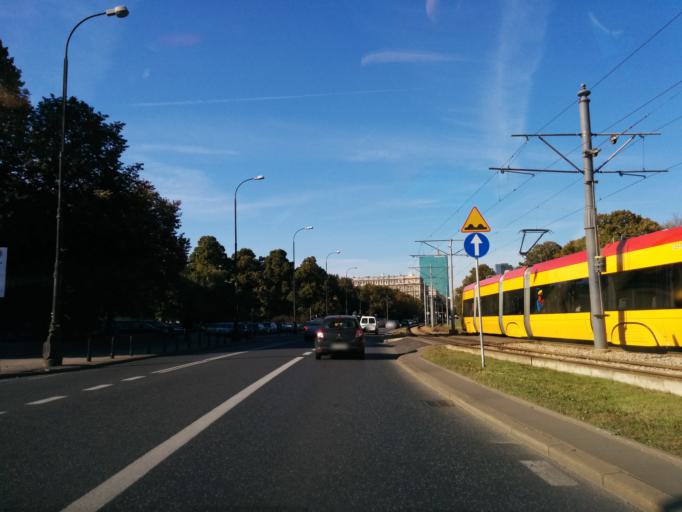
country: PL
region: Masovian Voivodeship
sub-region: Warszawa
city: Wola
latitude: 52.2459
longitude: 20.9999
